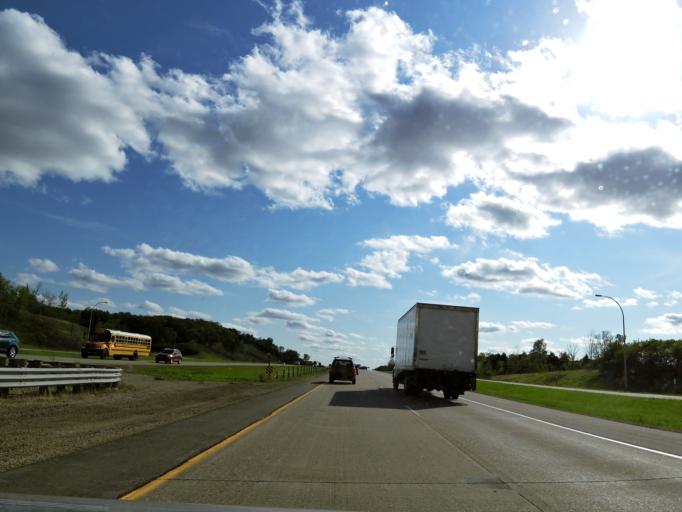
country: US
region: Minnesota
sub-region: Dakota County
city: Apple Valley
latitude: 44.7782
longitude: -93.2176
